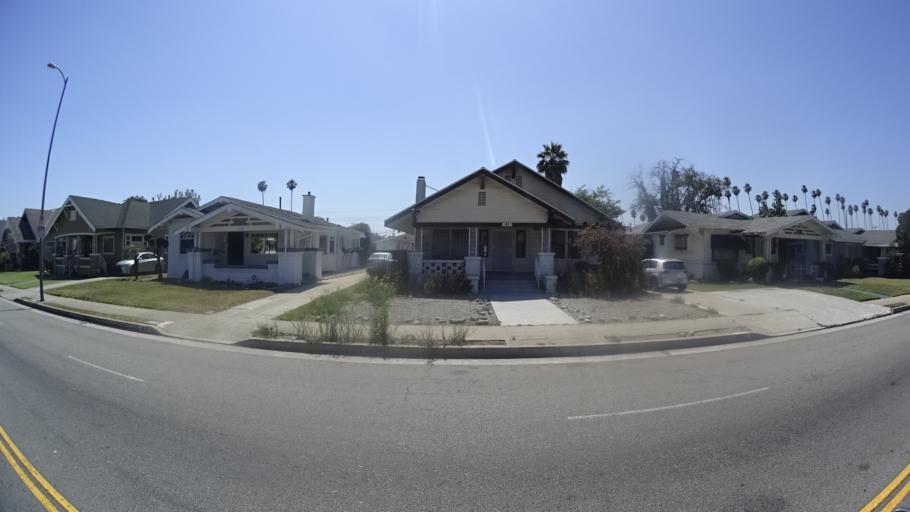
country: US
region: California
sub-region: Los Angeles County
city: View Park-Windsor Hills
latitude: 34.0225
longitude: -118.3177
